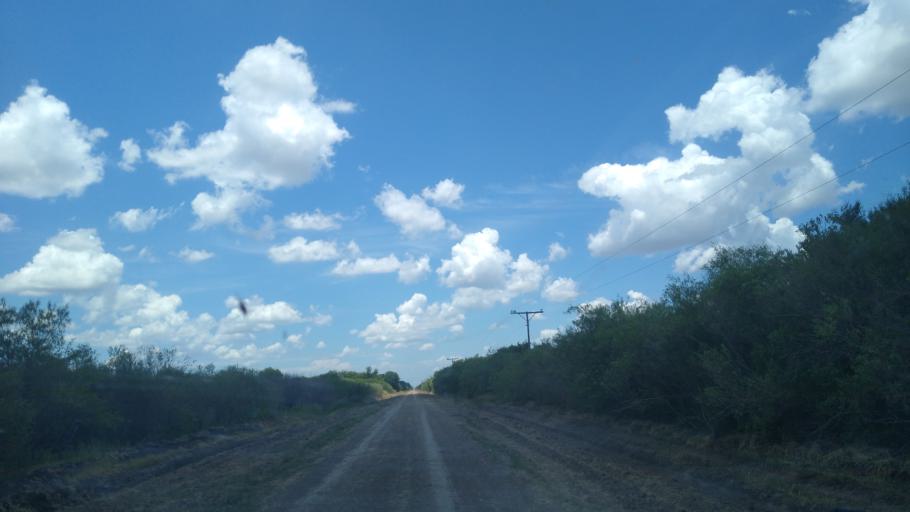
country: AR
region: Chaco
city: Presidencia Roque Saenz Pena
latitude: -26.7421
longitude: -60.3339
